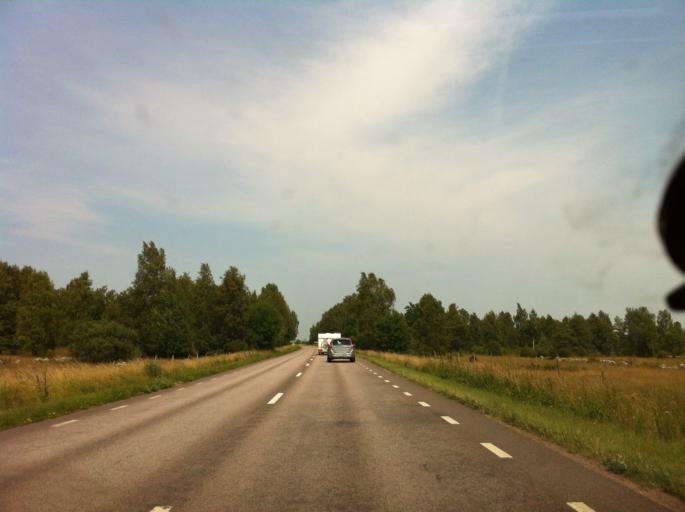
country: SE
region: Kalmar
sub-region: Borgholms Kommun
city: Borgholm
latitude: 56.9230
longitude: 16.7594
